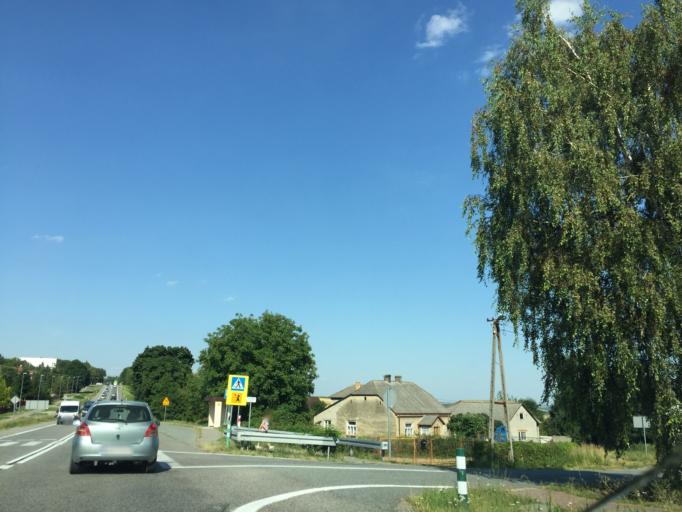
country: PL
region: Lesser Poland Voivodeship
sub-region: Powiat miechowski
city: Miechow
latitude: 50.4018
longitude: 20.0982
